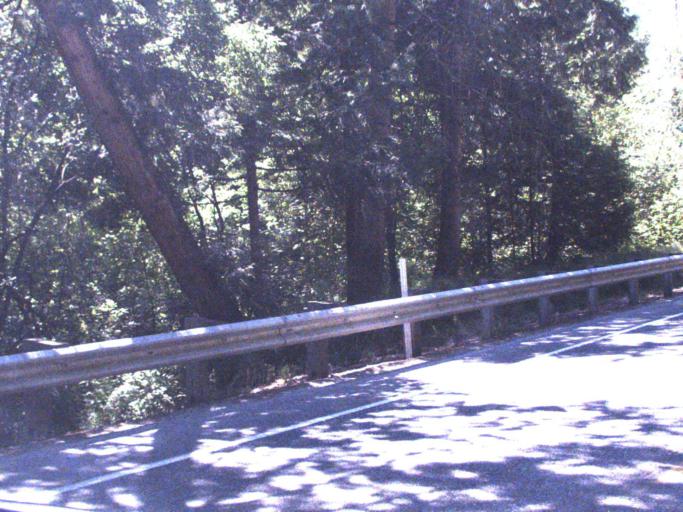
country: US
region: Washington
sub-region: King County
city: East Renton Highlands
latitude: 47.5077
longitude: -122.0888
